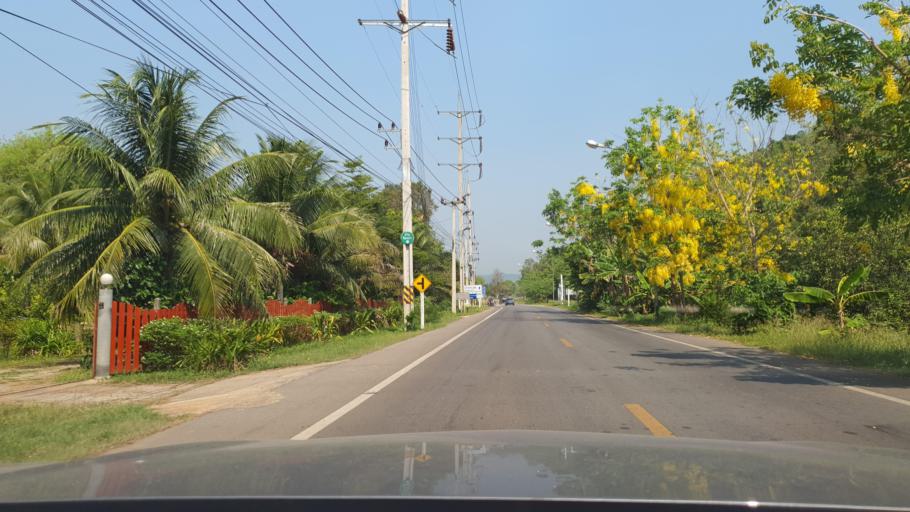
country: TH
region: Kanchanaburi
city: Sai Yok
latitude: 14.0933
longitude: 99.1794
